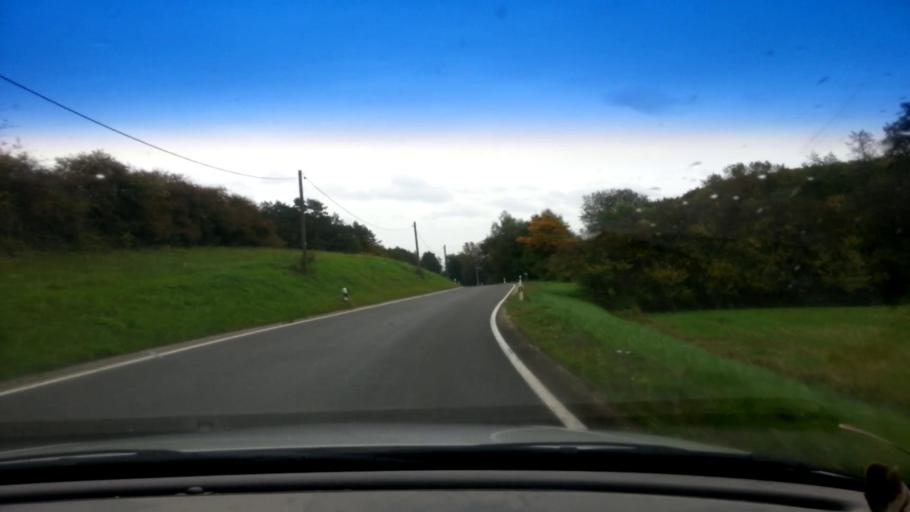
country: DE
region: Bavaria
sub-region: Upper Franconia
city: Lauter
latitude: 49.9872
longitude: 10.7622
